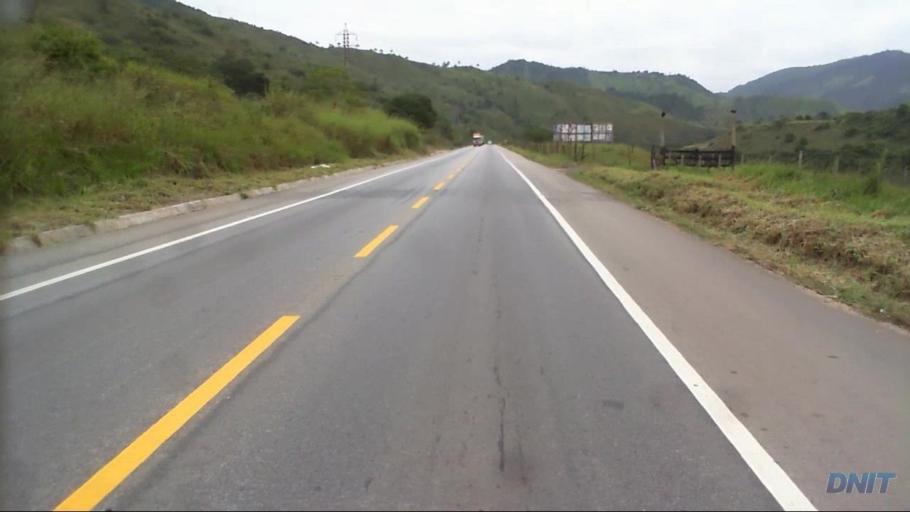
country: BR
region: Minas Gerais
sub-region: Timoteo
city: Timoteo
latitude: -19.6146
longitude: -42.7715
